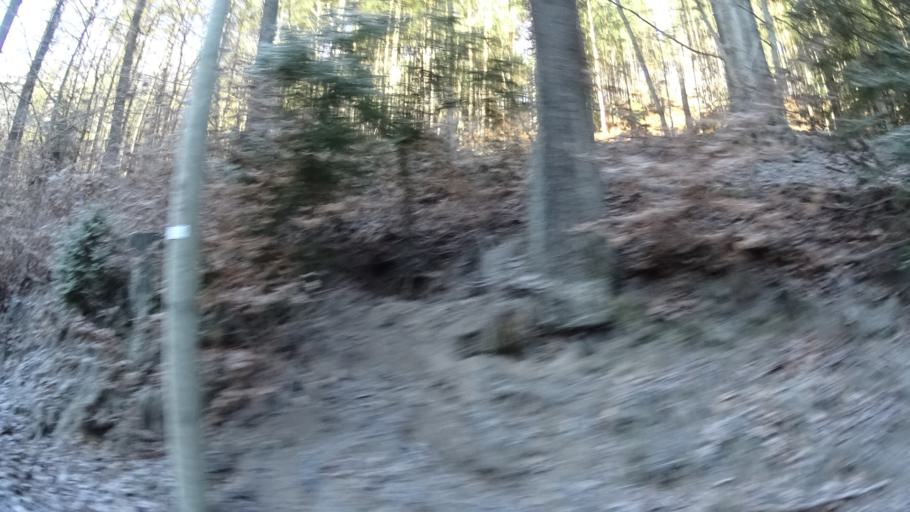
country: DE
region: Thuringia
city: Seitenroda
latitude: 50.7834
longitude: 11.6226
